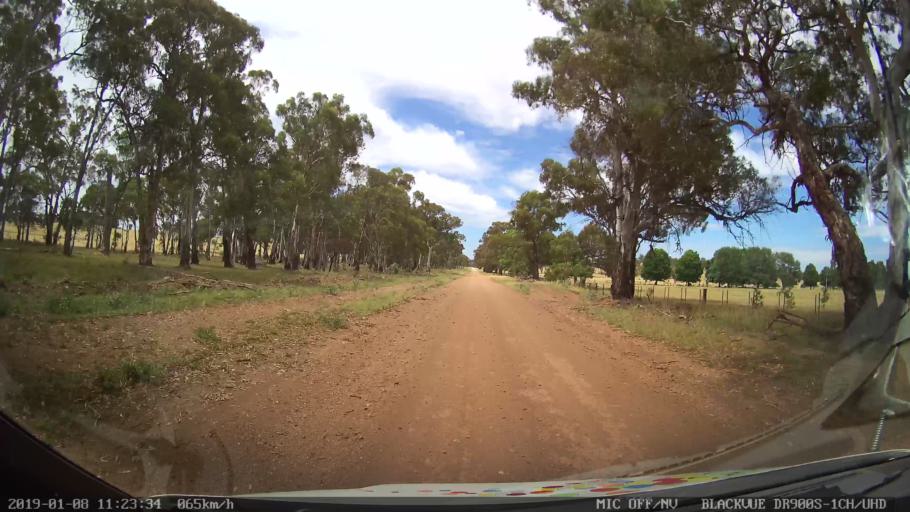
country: AU
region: New South Wales
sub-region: Guyra
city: Guyra
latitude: -30.2565
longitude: 151.5588
